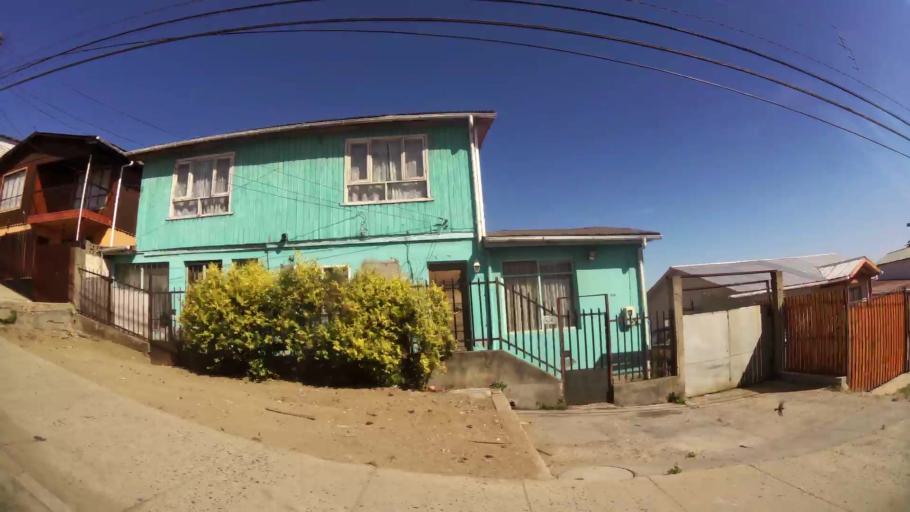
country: CL
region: Valparaiso
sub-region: Provincia de Valparaiso
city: Valparaiso
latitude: -33.0454
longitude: -71.6397
